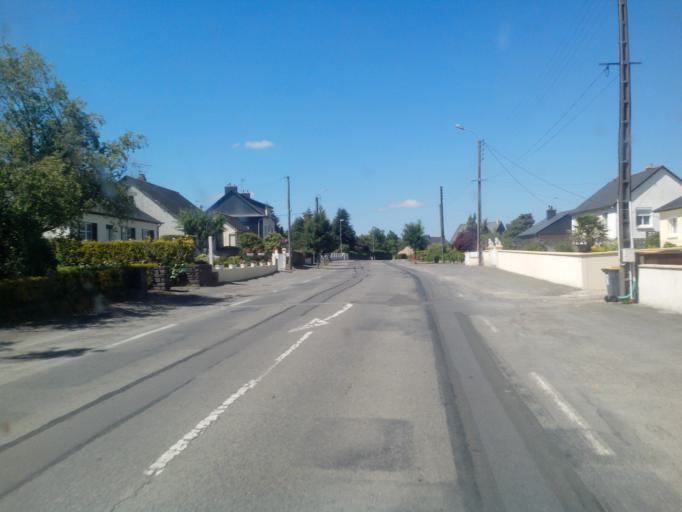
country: FR
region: Brittany
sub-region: Departement d'Ille-et-Vilaine
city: Saint-Meen-le-Grand
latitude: 48.1807
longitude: -2.1996
